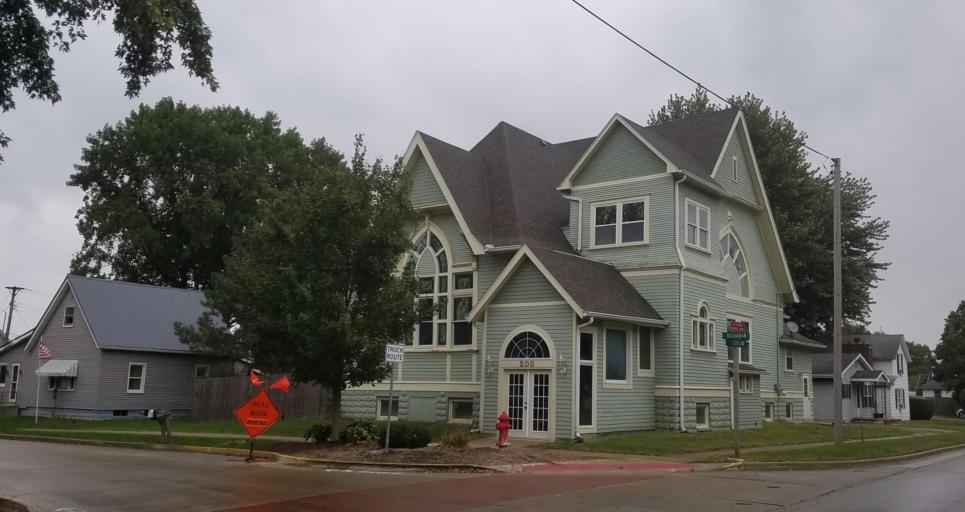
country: US
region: Illinois
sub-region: McLean County
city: Heyworth
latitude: 40.3117
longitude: -88.9783
